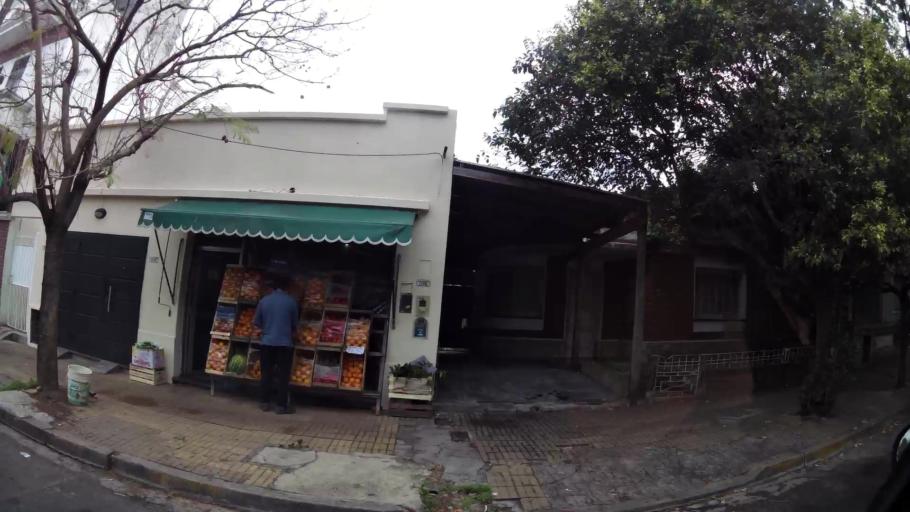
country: AR
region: Buenos Aires
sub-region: Partido de Quilmes
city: Quilmes
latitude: -34.7587
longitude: -58.2100
